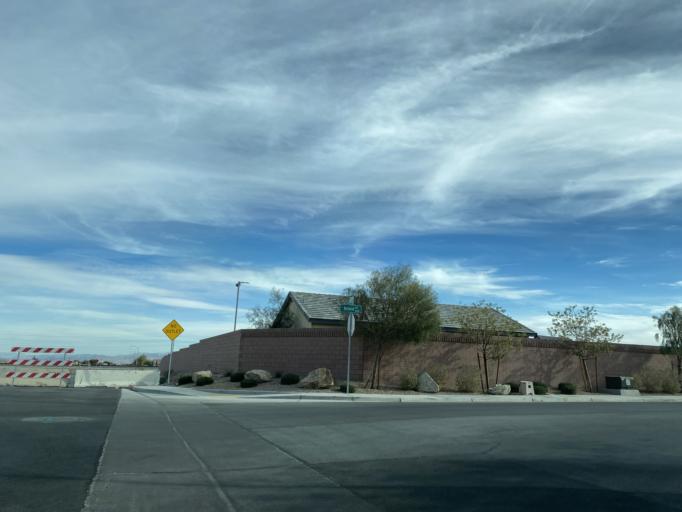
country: US
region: Nevada
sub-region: Clark County
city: Enterprise
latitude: 36.0421
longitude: -115.2192
